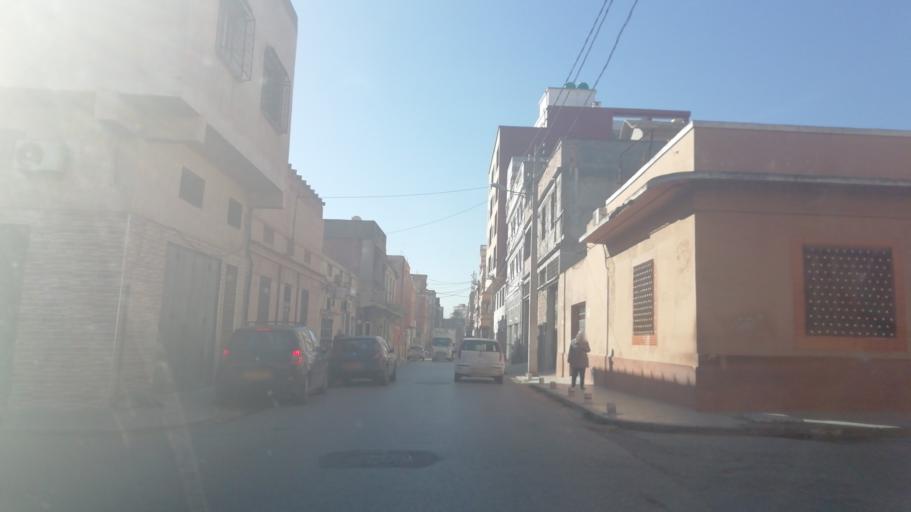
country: DZ
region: Oran
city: Oran
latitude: 35.6835
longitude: -0.6536
